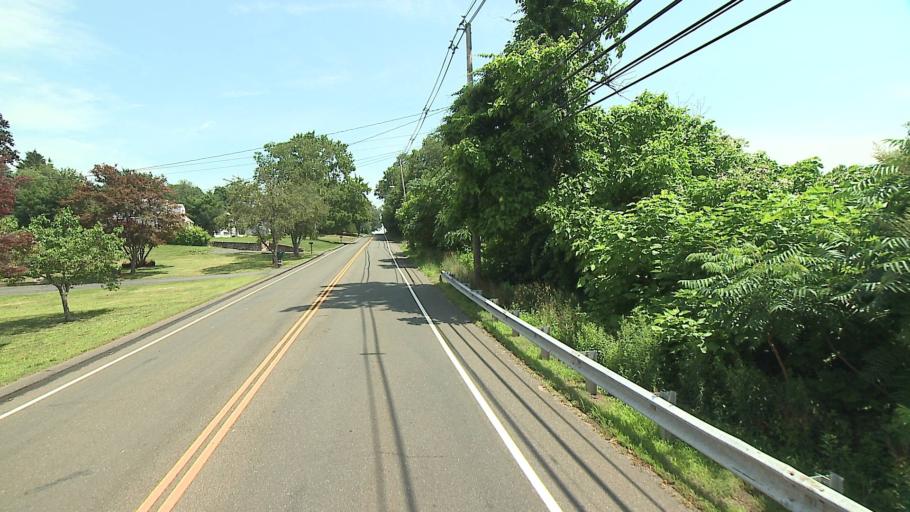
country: US
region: Connecticut
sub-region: New Haven County
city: Wallingford Center
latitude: 41.4469
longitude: -72.7964
